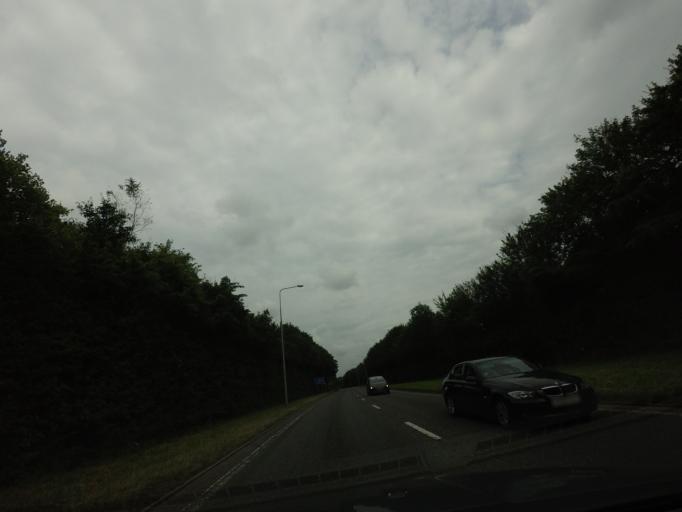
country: GB
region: England
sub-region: Telford and Wrekin
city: Madeley
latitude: 52.6460
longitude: -2.4502
